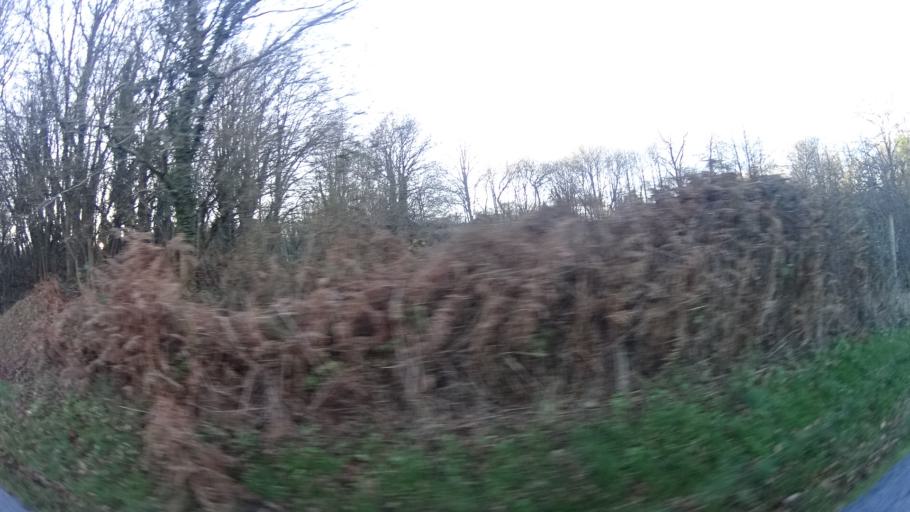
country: FR
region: Brittany
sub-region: Departement du Morbihan
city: Saint-Jean-la-Poterie
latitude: 47.6515
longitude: -2.1231
